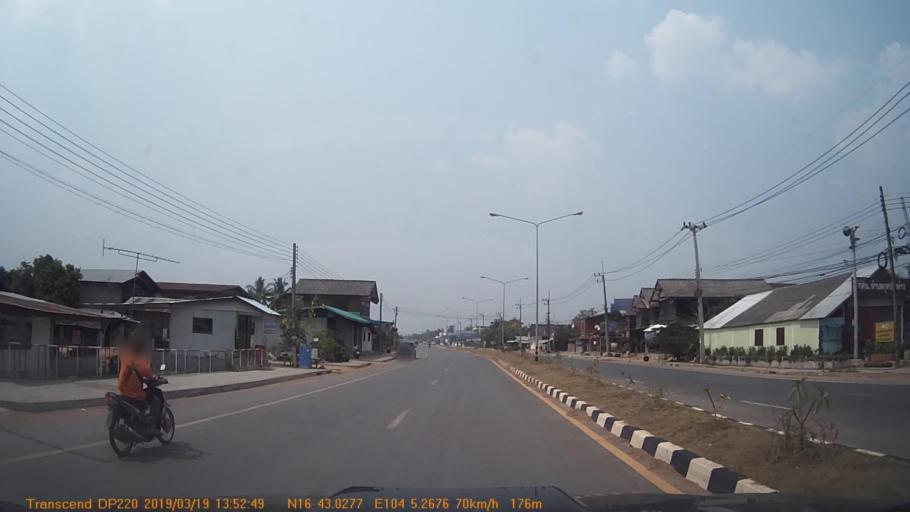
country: TH
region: Kalasin
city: Khao Wong
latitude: 16.7175
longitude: 104.0877
